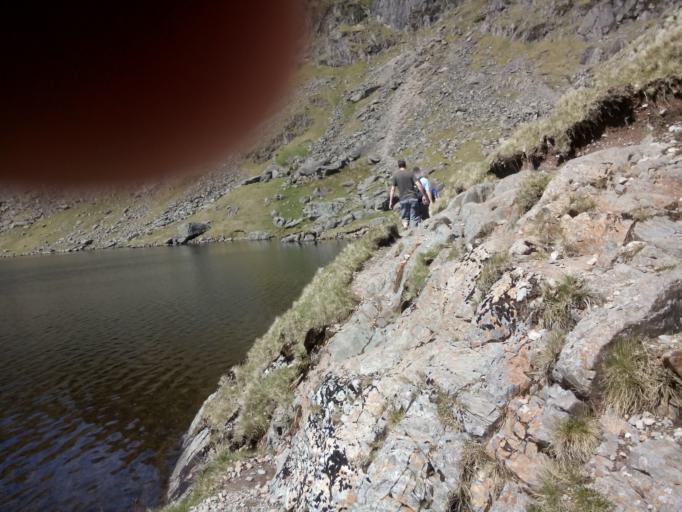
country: GB
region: England
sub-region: Cumbria
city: Ambleside
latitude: 54.4609
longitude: -3.1000
